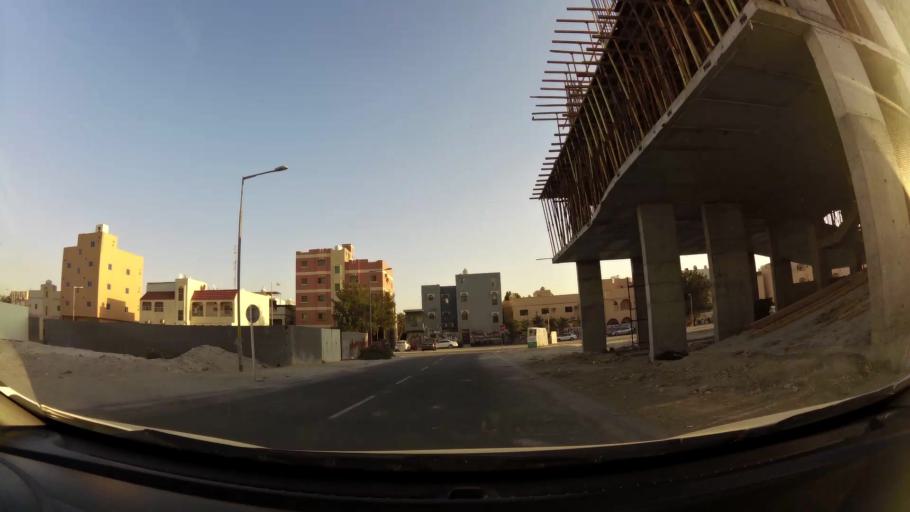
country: BH
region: Manama
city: Jidd Hafs
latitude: 26.2253
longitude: 50.5571
